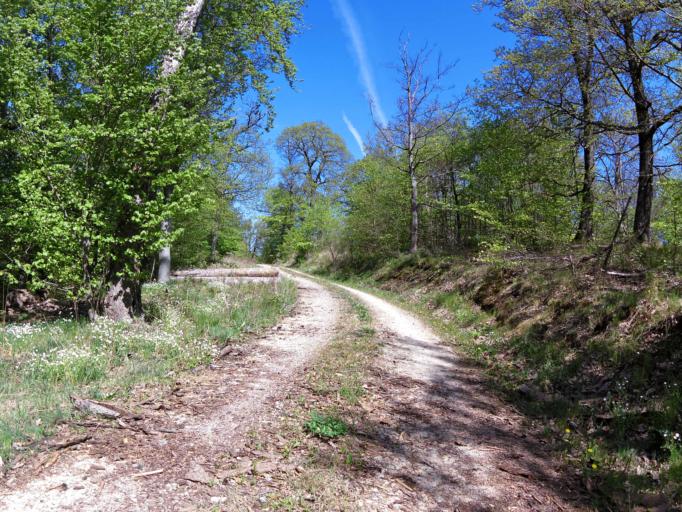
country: DE
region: Thuringia
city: Wolfsburg-Unkeroda
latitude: 50.9622
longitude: 10.2631
